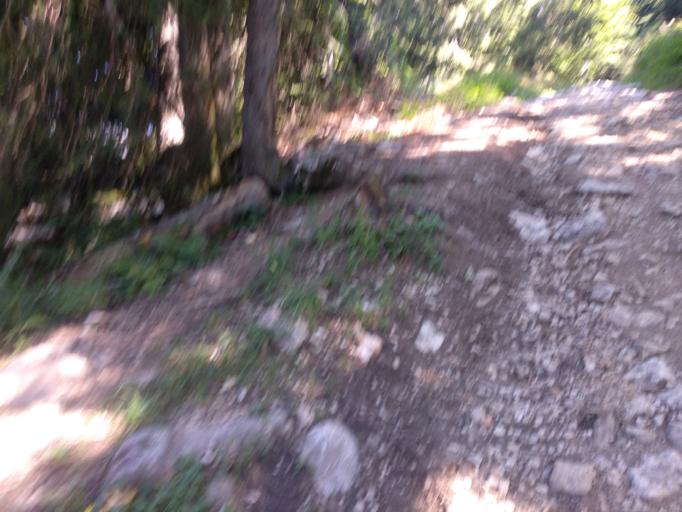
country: FR
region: Rhone-Alpes
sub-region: Departement de l'Isere
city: Le Sappey-en-Chartreuse
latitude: 45.2897
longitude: 5.7738
